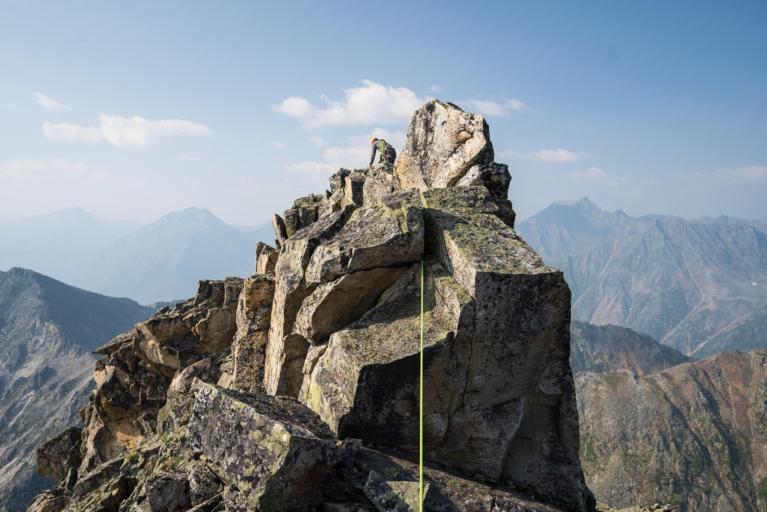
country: RU
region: Transbaikal Territory
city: Kuanda
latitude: 56.7900
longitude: 116.8197
